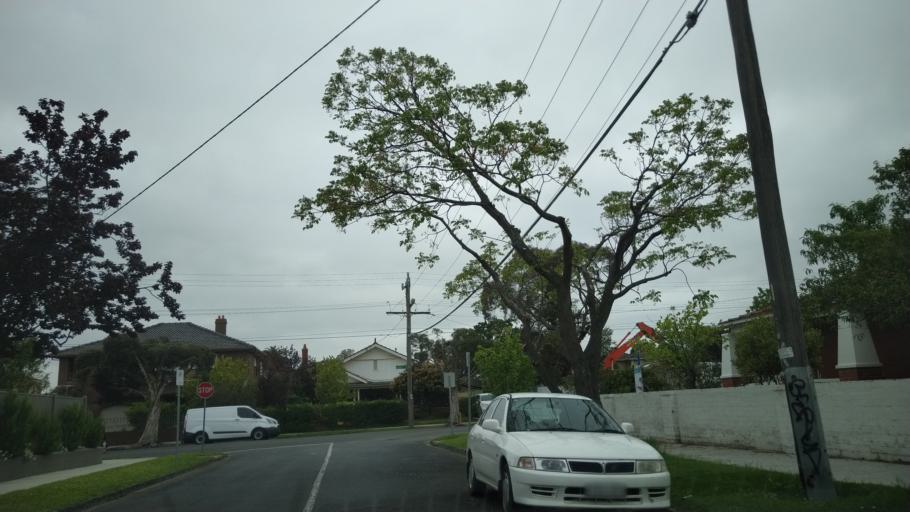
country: AU
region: Victoria
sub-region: Glen Eira
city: Murrumbeena
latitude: -37.8876
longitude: 145.0696
